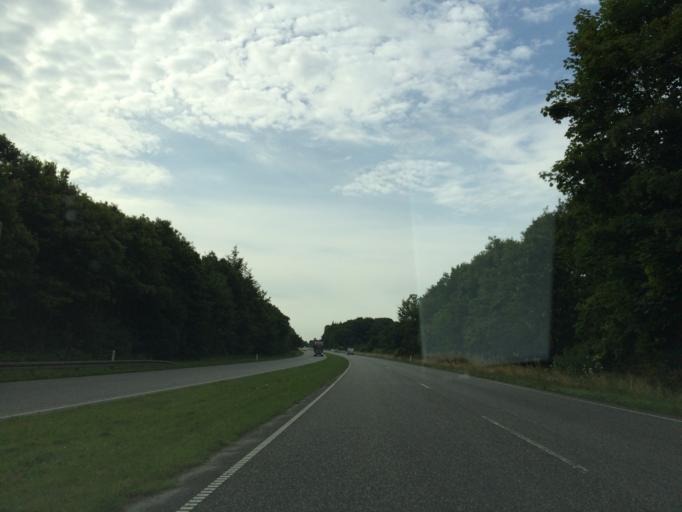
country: DK
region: South Denmark
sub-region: Kolding Kommune
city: Kolding
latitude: 55.5263
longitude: 9.4967
